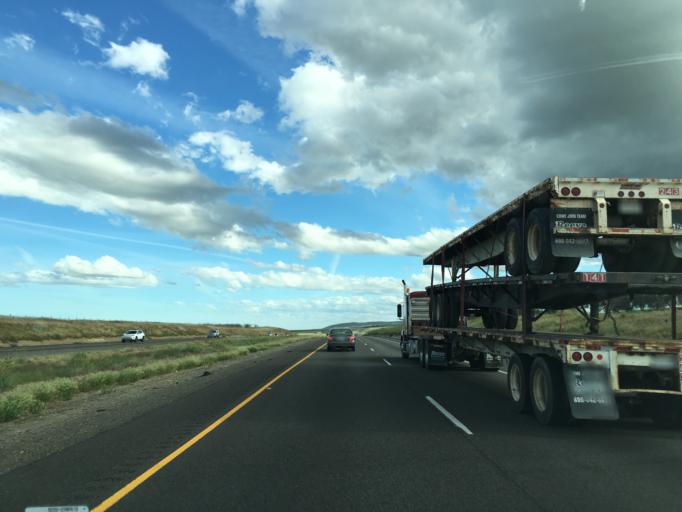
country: US
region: California
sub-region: Merced County
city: Los Banos
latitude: 37.0117
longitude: -120.9264
